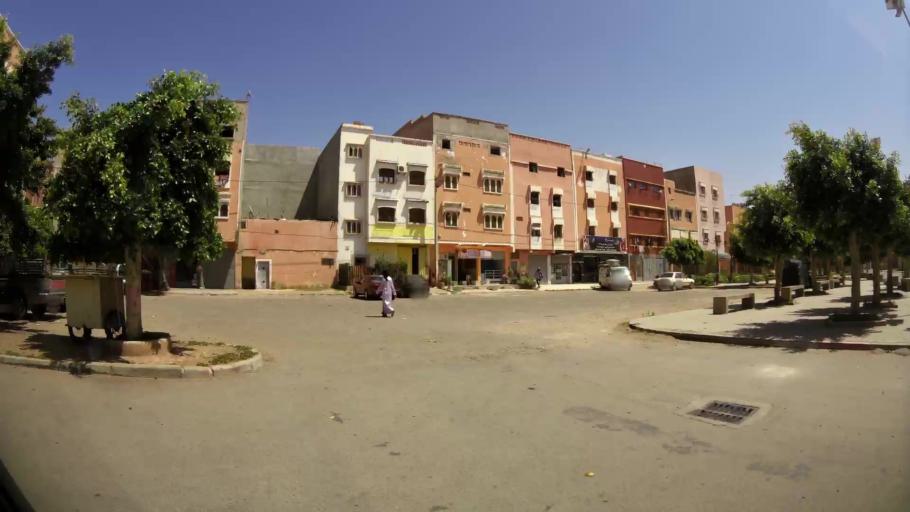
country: MA
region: Souss-Massa-Draa
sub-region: Inezgane-Ait Mellou
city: Inezgane
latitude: 30.3433
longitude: -9.4856
